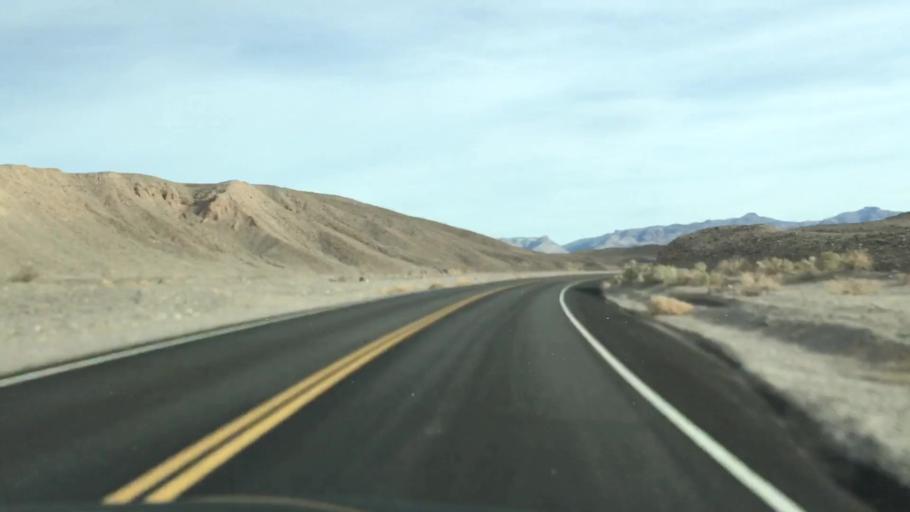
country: US
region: Nevada
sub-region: Nye County
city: Beatty
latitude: 36.6547
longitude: -117.0261
